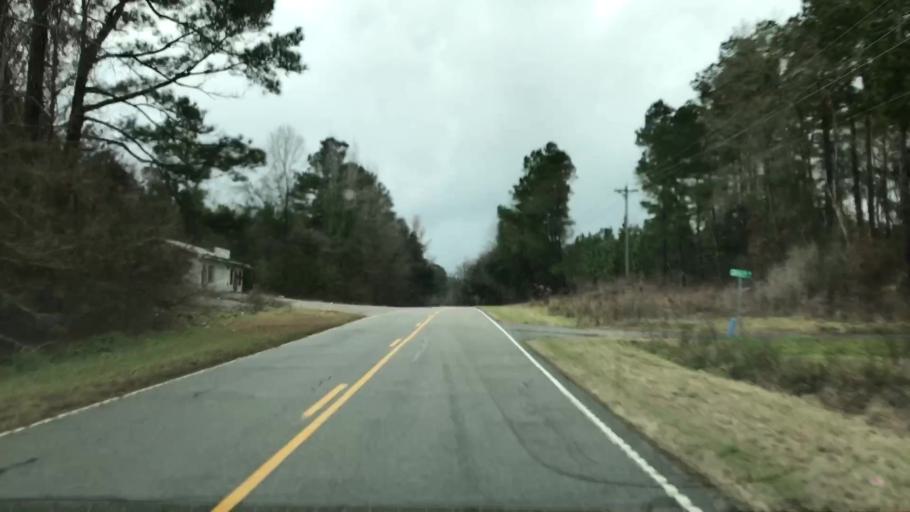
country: US
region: South Carolina
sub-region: Florence County
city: Johnsonville
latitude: 33.6622
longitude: -79.4109
